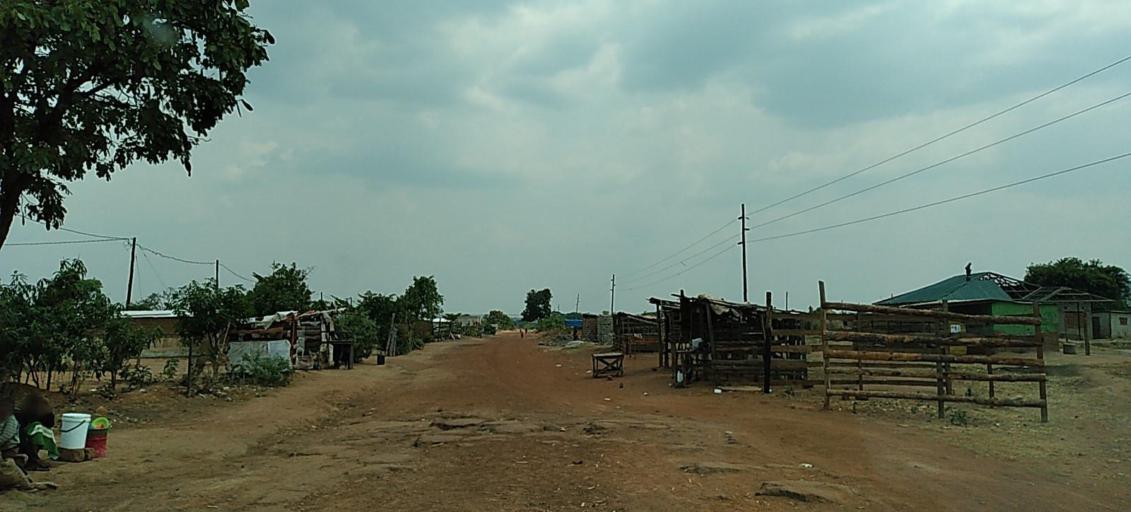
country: ZM
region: Copperbelt
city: Kalulushi
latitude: -12.8654
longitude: 28.0780
